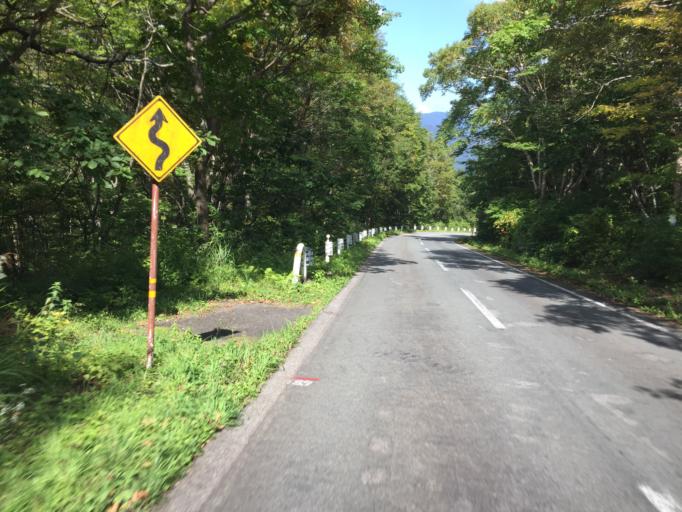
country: JP
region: Fukushima
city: Inawashiro
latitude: 37.6391
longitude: 140.0521
